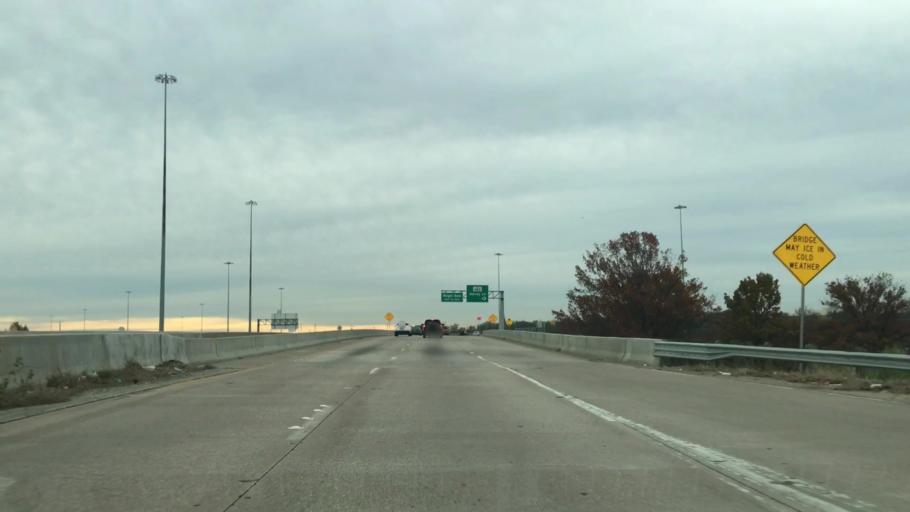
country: US
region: Texas
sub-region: Dallas County
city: Irving
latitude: 32.8393
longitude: -96.9059
